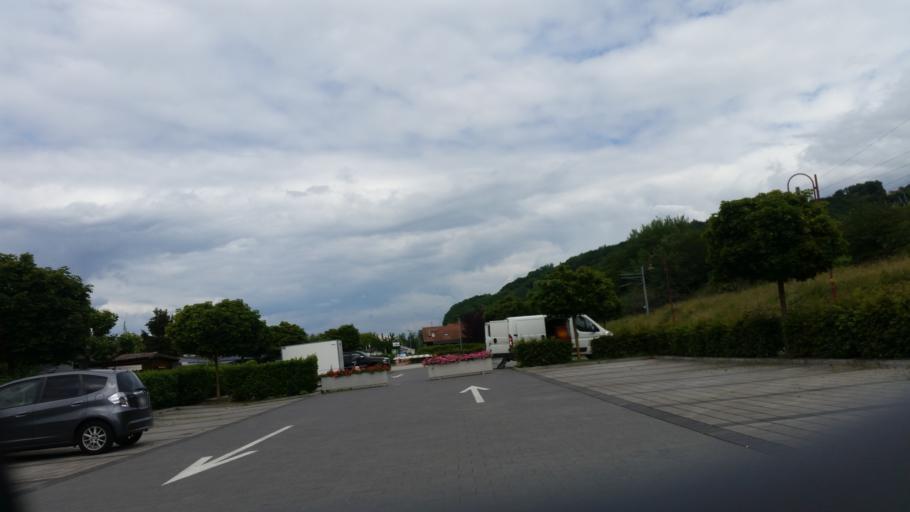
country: CH
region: Vaud
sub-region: Jura-Nord vaudois District
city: Yvonand
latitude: 46.8183
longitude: 6.7879
